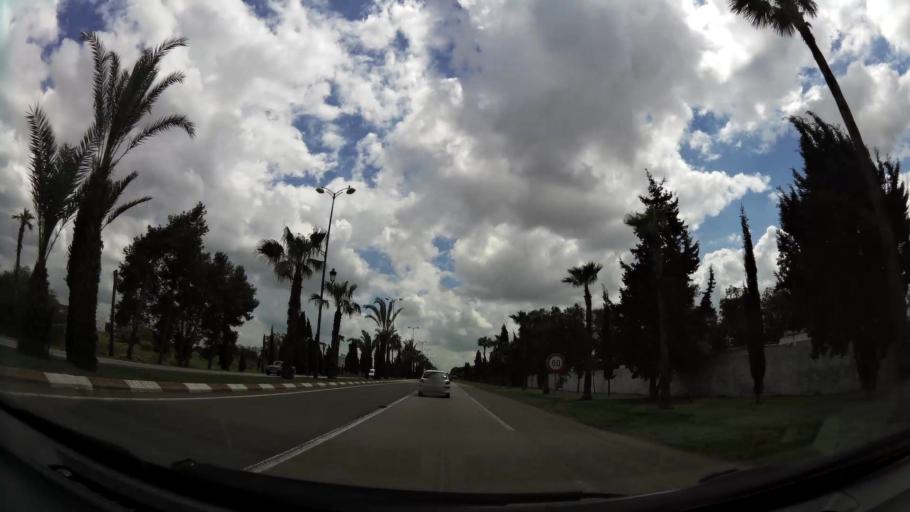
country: MA
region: Chaouia-Ouardigha
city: Nouaseur
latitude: 33.3975
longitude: -7.5691
